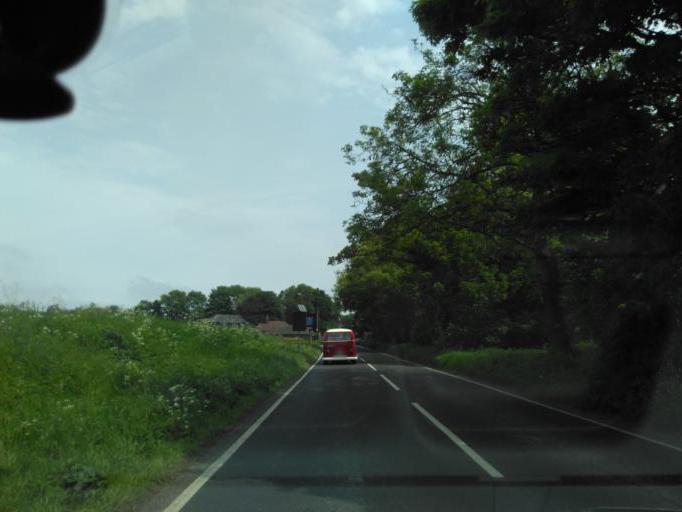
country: GB
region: England
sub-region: Kent
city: Canterbury
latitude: 51.2381
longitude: 1.0711
